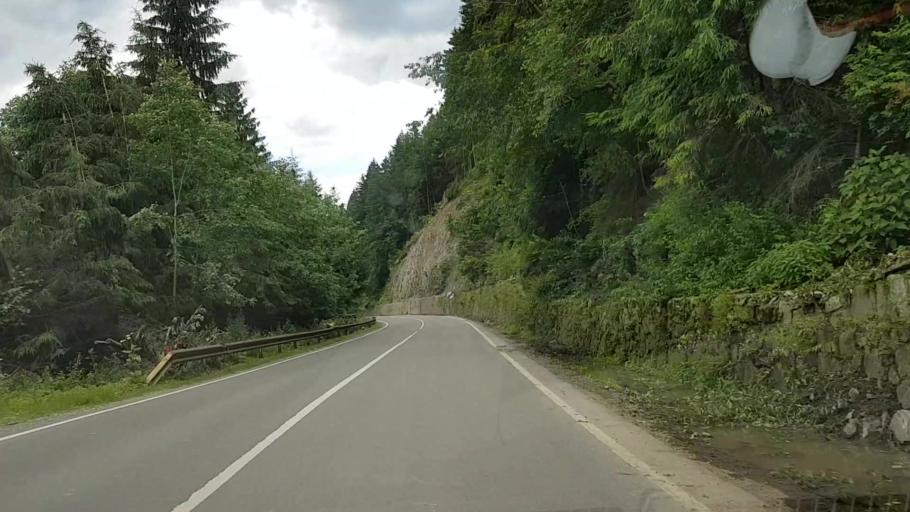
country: RO
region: Neamt
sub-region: Comuna Poiana Teiului
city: Poiana Teiului
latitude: 47.0932
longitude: 25.9487
